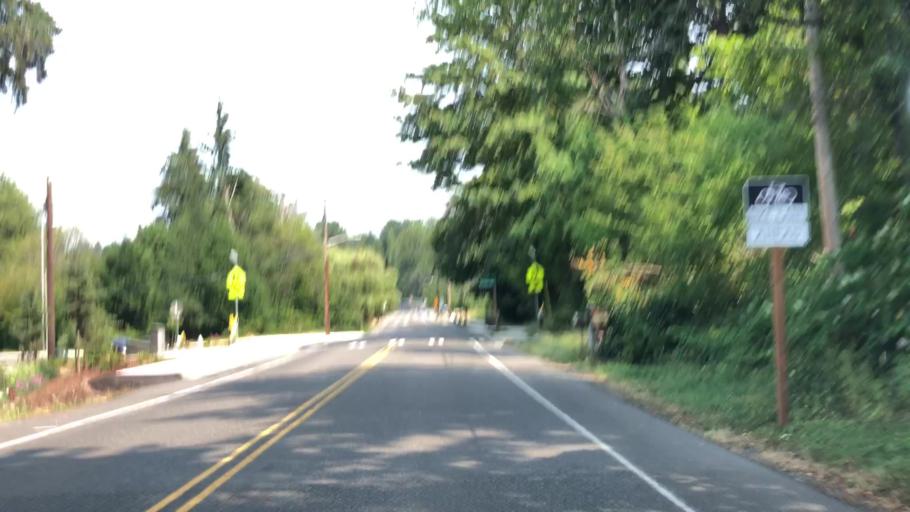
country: US
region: Washington
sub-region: King County
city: Kenmore
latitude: 47.7746
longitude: -122.2540
